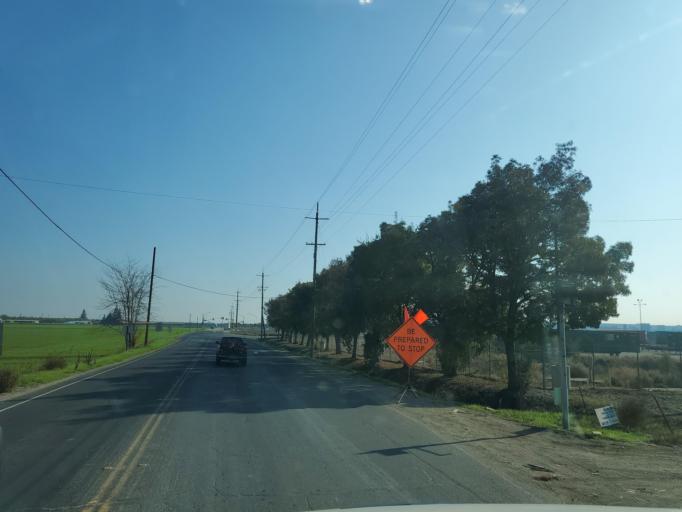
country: US
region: California
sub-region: San Joaquin County
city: French Camp
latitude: 37.8556
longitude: -121.2641
